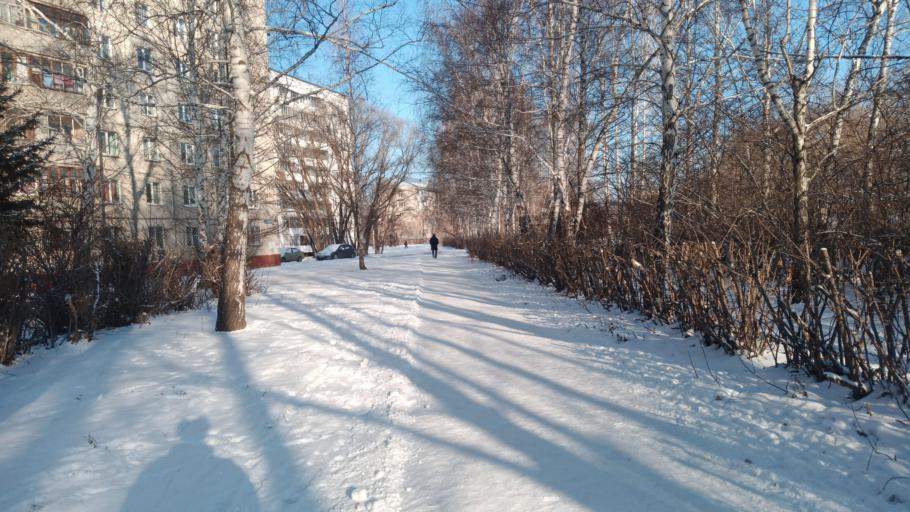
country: RU
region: Altai Krai
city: Yuzhnyy
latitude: 53.2485
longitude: 83.6874
